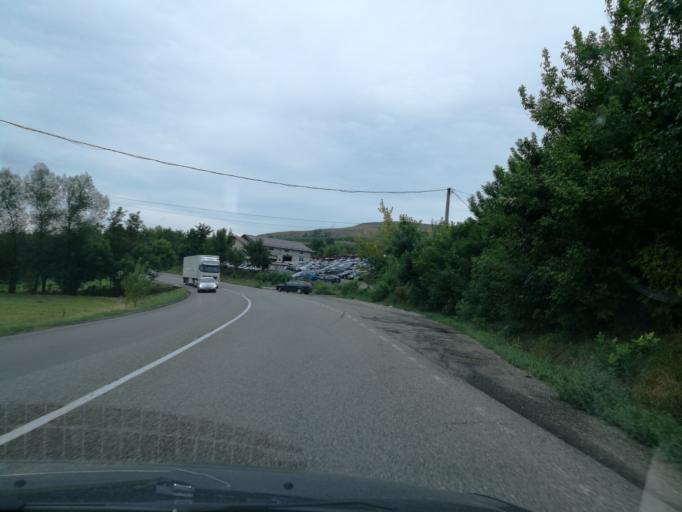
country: RO
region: Suceava
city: Bunesti-Regat
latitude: 47.5026
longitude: 26.2848
